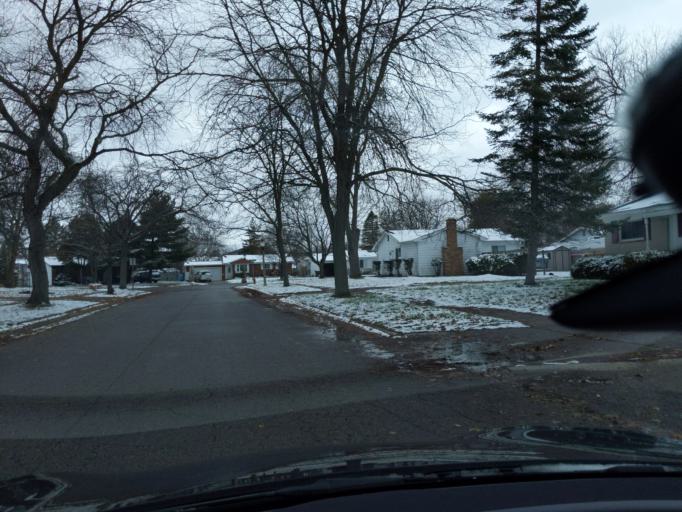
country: US
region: Michigan
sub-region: Eaton County
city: Waverly
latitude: 42.6844
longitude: -84.5998
